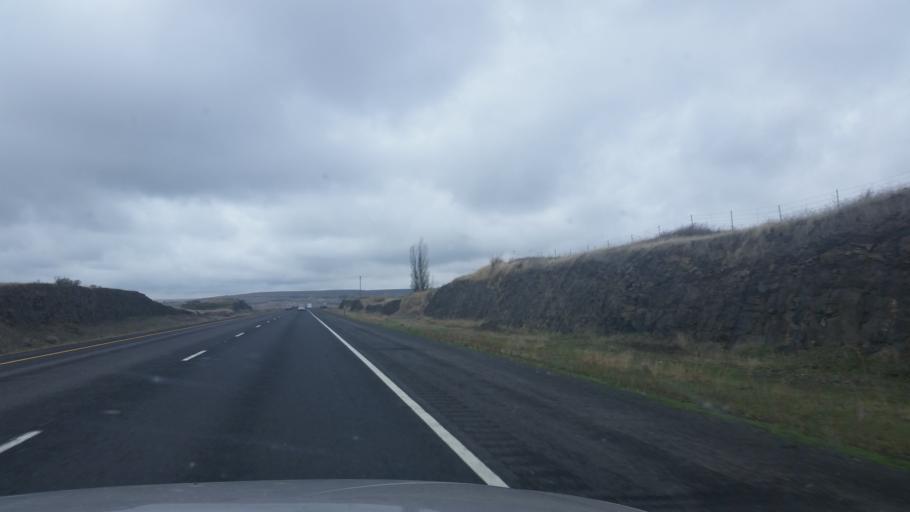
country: US
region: Washington
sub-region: Lincoln County
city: Davenport
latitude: 47.3030
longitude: -117.9930
